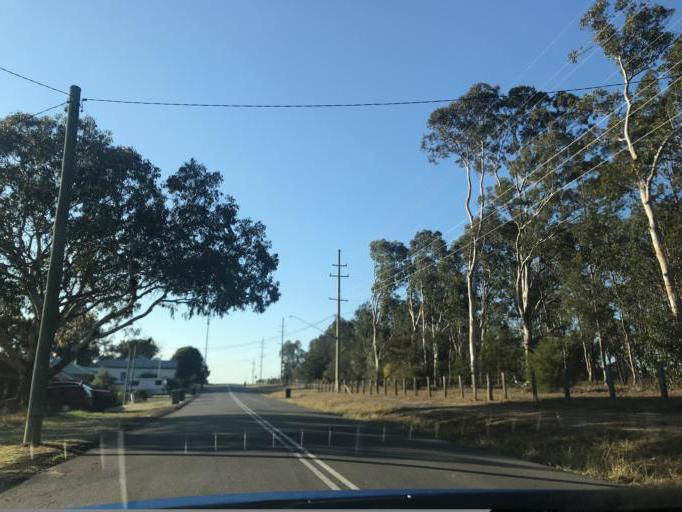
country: AU
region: New South Wales
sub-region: Cessnock
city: Cessnock
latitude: -32.9049
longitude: 151.2830
